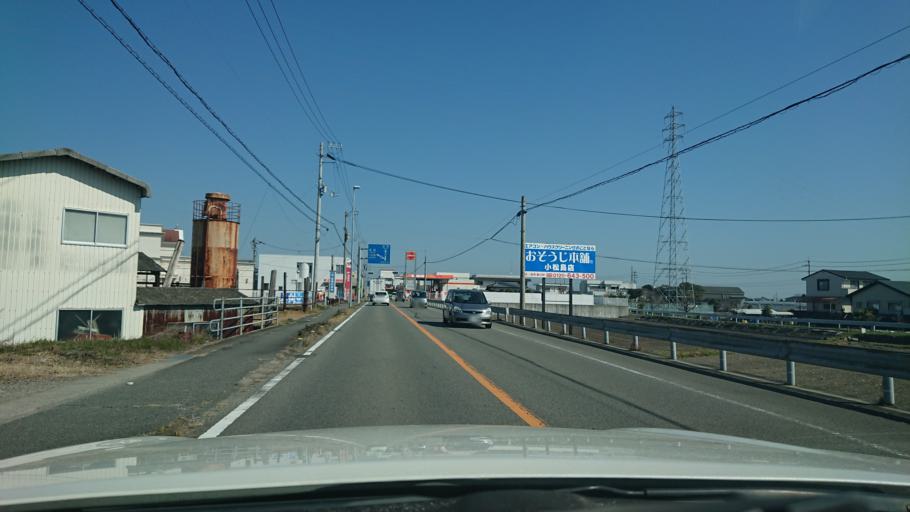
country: JP
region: Tokushima
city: Anan
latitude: 33.9467
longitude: 134.6253
